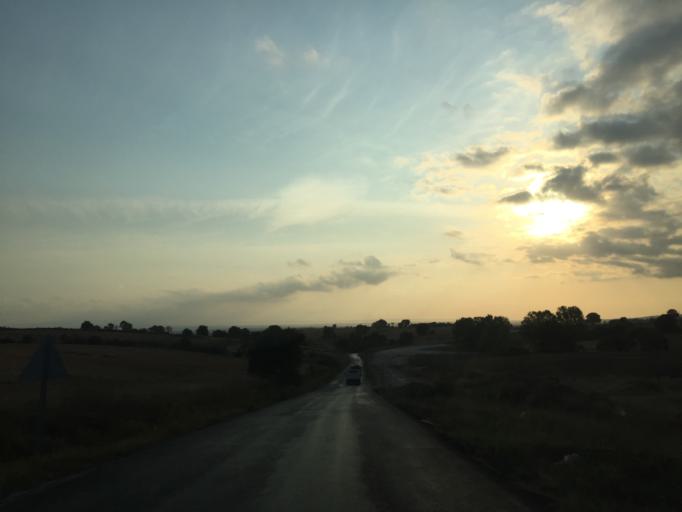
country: TR
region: Balikesir
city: Sevketiye
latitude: 40.1168
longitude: 27.7852
